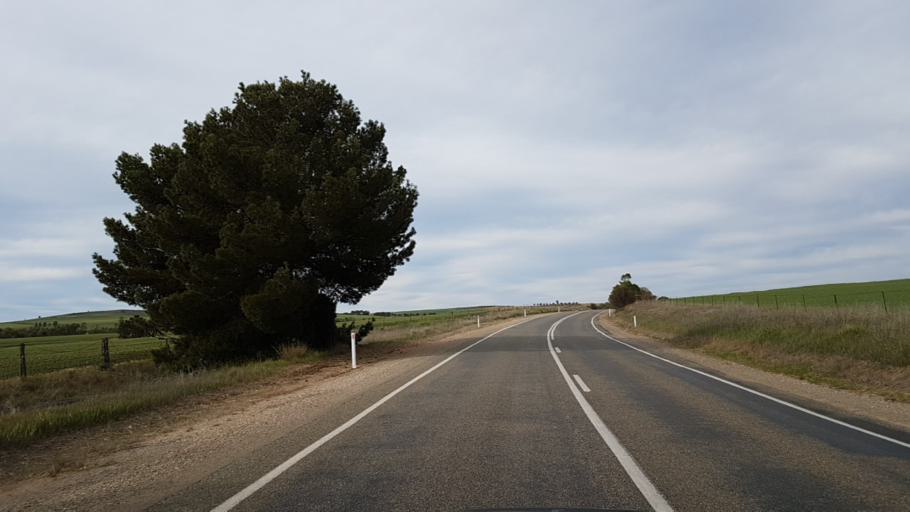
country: AU
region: South Australia
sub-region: Northern Areas
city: Jamestown
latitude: -33.2160
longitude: 138.4167
